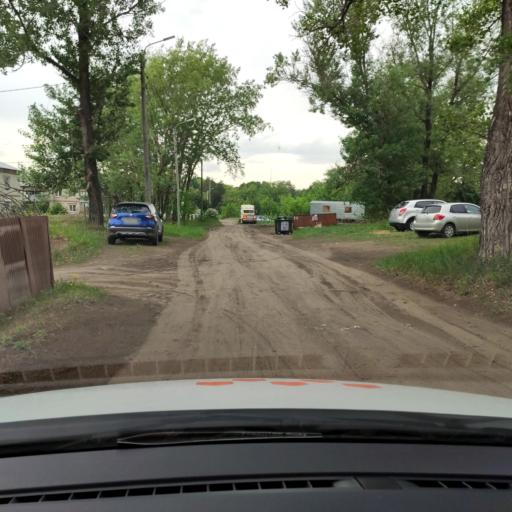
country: RU
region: Tatarstan
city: Staroye Arakchino
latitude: 55.8068
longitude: 48.9638
